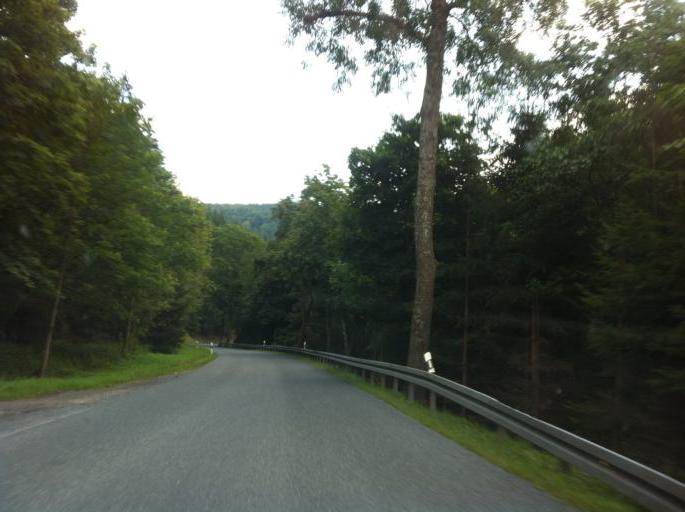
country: DE
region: Thuringia
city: Katzhutte
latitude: 50.5344
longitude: 11.0714
